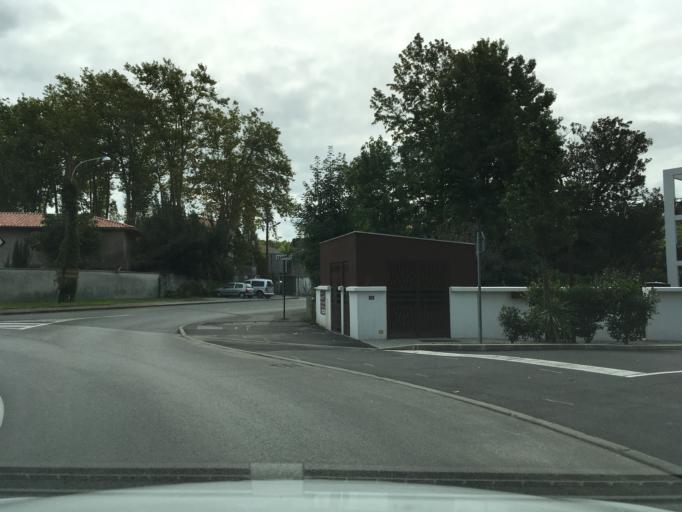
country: FR
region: Aquitaine
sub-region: Departement des Pyrenees-Atlantiques
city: Bayonne
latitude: 43.4809
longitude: -1.4608
